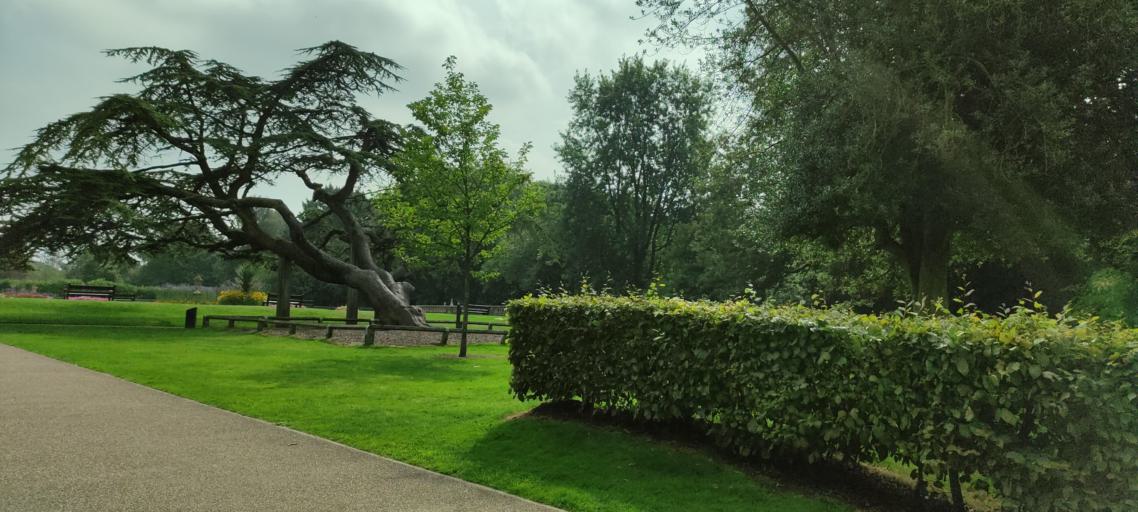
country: GB
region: England
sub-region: Lancashire
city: Leyland
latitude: 53.6823
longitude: -2.7031
